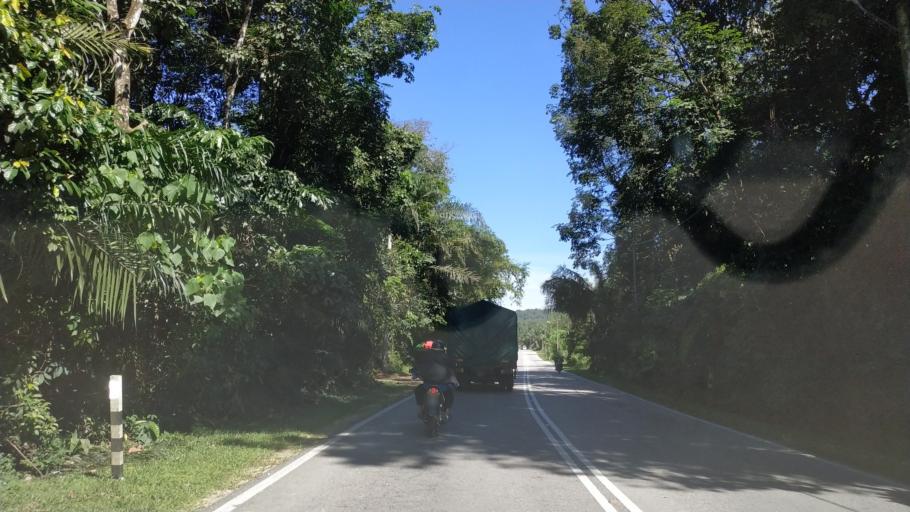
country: MY
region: Kedah
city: Kulim
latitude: 5.3108
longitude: 100.5402
